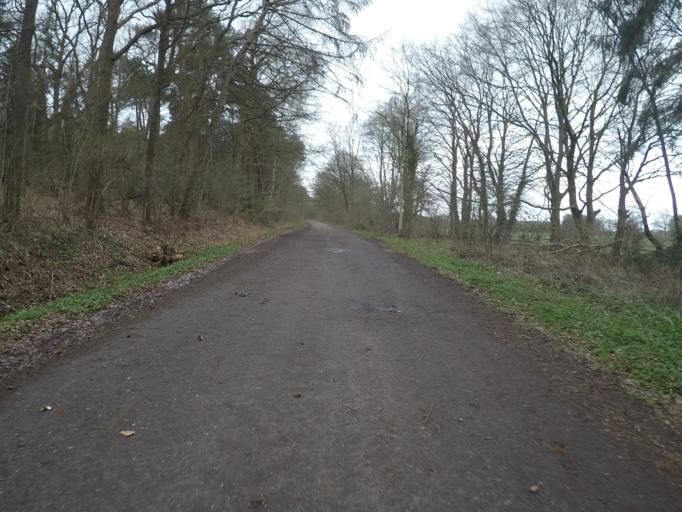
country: DE
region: Lower Saxony
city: Langen
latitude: 53.6062
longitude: 8.6679
